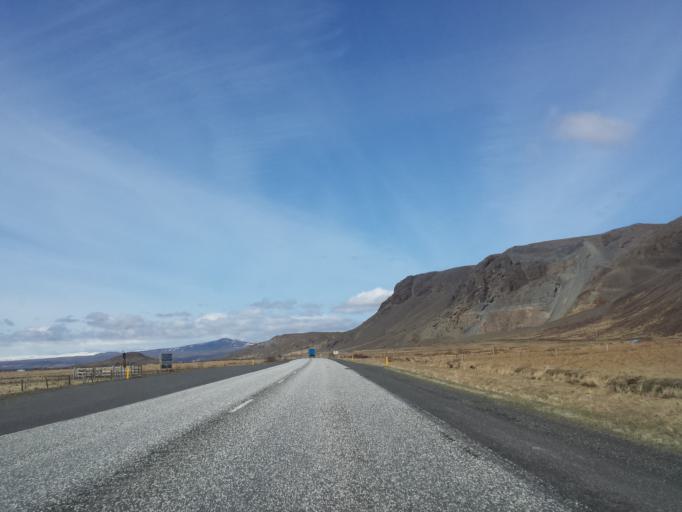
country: IS
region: South
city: Selfoss
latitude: 63.9526
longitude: -21.0321
